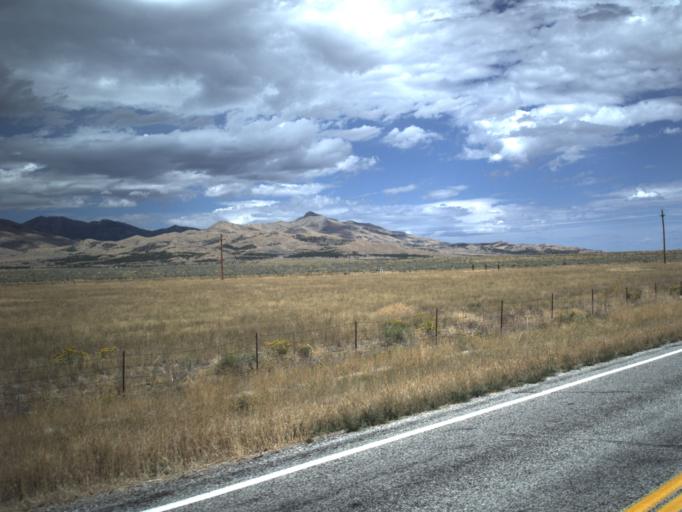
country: US
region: Idaho
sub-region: Oneida County
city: Malad City
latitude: 41.9637
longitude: -113.0625
